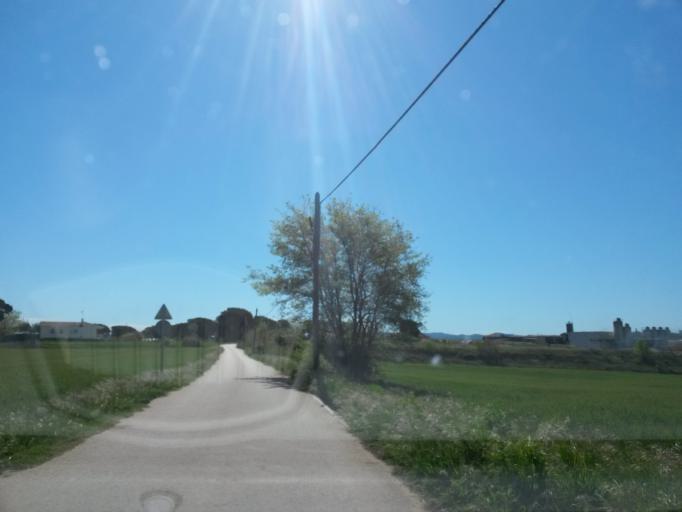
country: ES
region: Catalonia
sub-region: Provincia de Girona
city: Riudellots de la Selva
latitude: 41.9033
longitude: 2.7838
